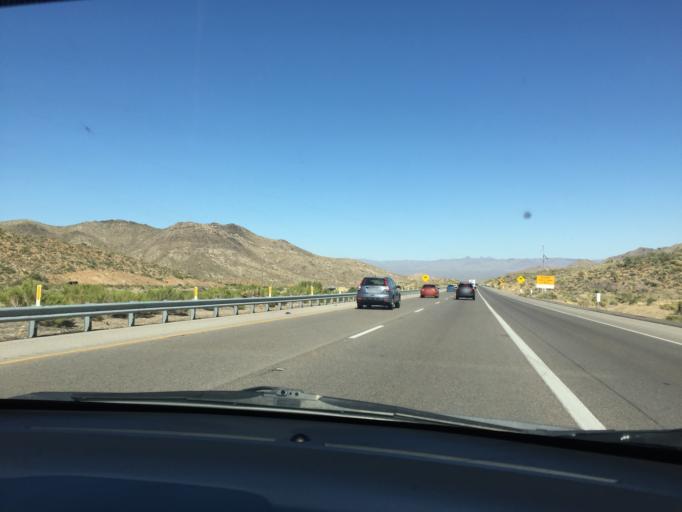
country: US
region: Nevada
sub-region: Clark County
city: Sandy Valley
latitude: 35.4682
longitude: -115.4956
